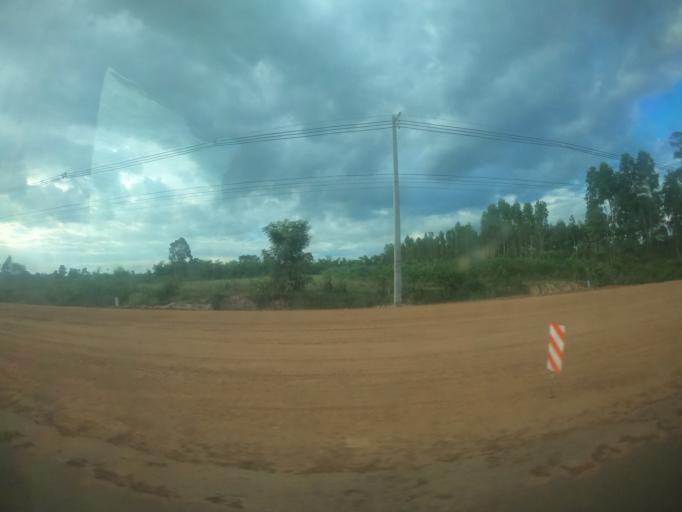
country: TH
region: Surin
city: Kap Choeng
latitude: 14.4577
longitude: 103.6717
